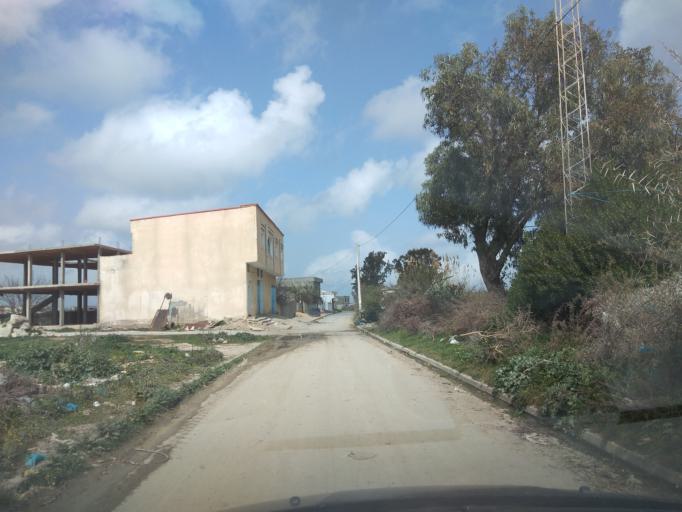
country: TN
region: Ariana
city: Qal'at al Andalus
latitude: 37.0647
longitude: 10.1253
